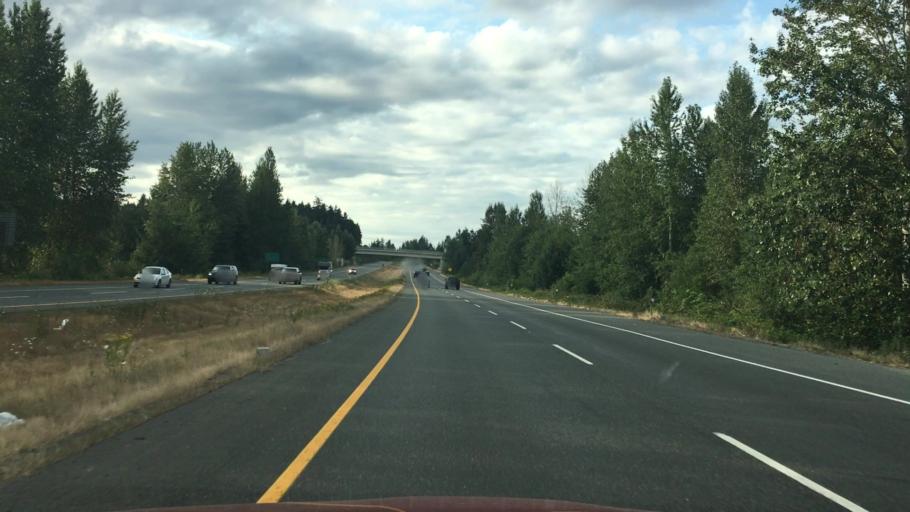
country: CA
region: British Columbia
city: Nanaimo
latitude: 49.1760
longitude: -123.9837
